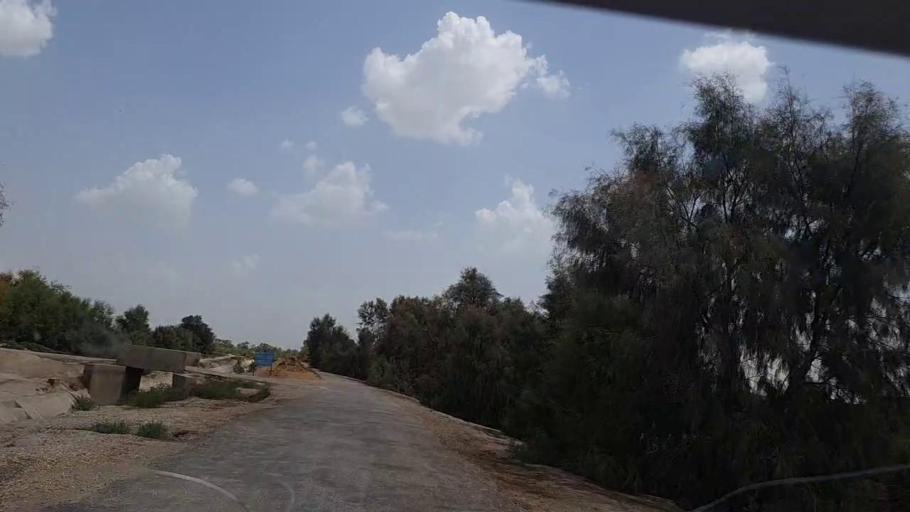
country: PK
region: Sindh
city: Bhan
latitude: 26.5141
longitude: 67.6398
